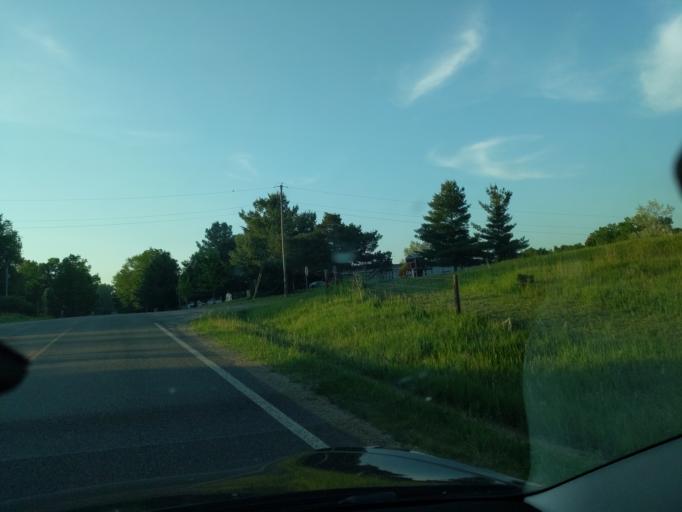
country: US
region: Michigan
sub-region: Barry County
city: Nashville
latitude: 42.5522
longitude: -85.0939
